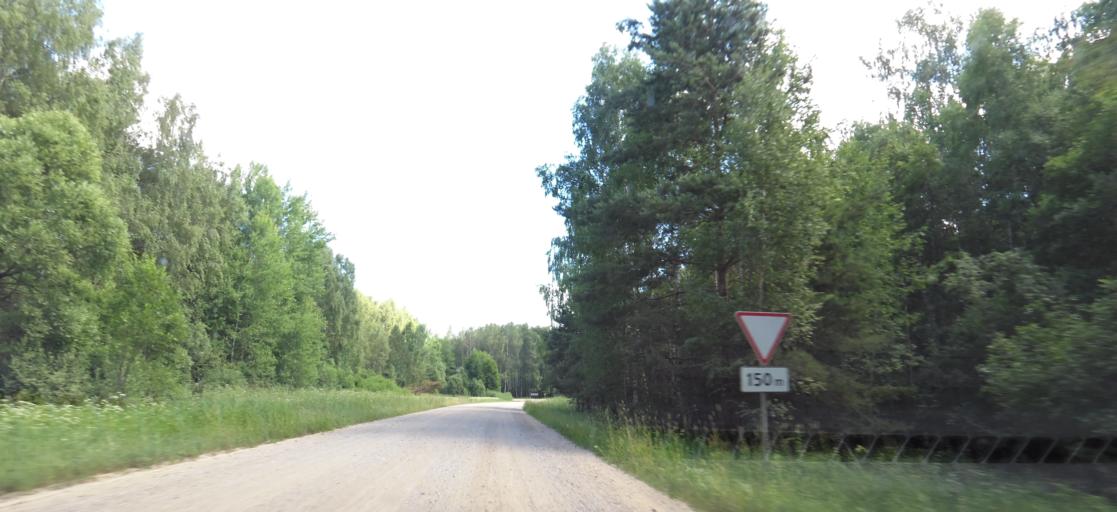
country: LT
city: Obeliai
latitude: 56.0430
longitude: 24.9578
